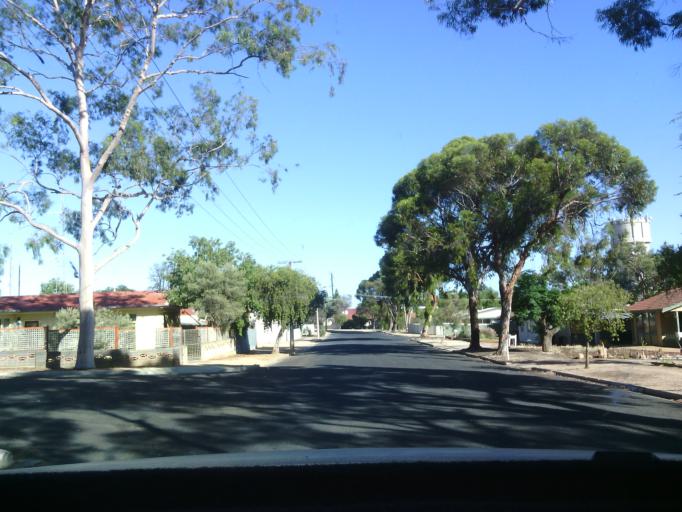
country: AU
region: South Australia
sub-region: Berri and Barmera
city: Berri
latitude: -34.2747
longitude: 140.5994
